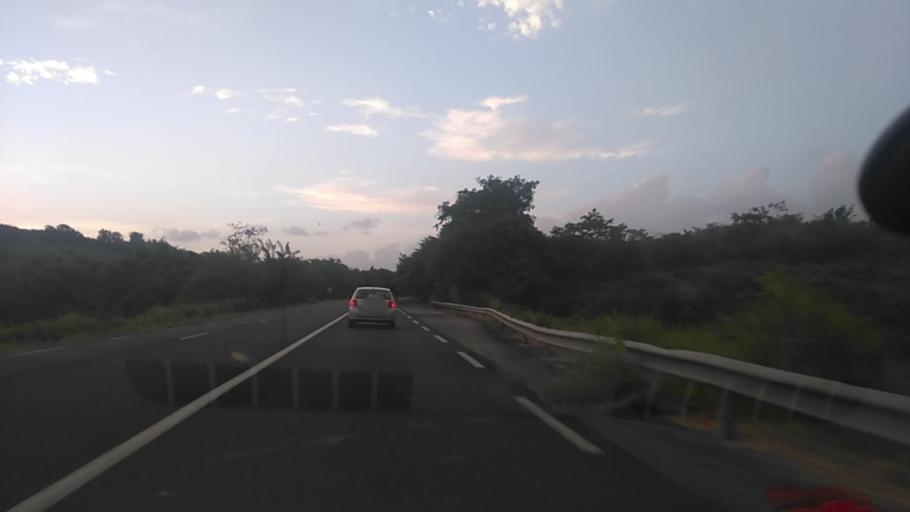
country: MQ
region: Martinique
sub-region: Martinique
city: Sainte-Luce
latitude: 14.4829
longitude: -60.9650
